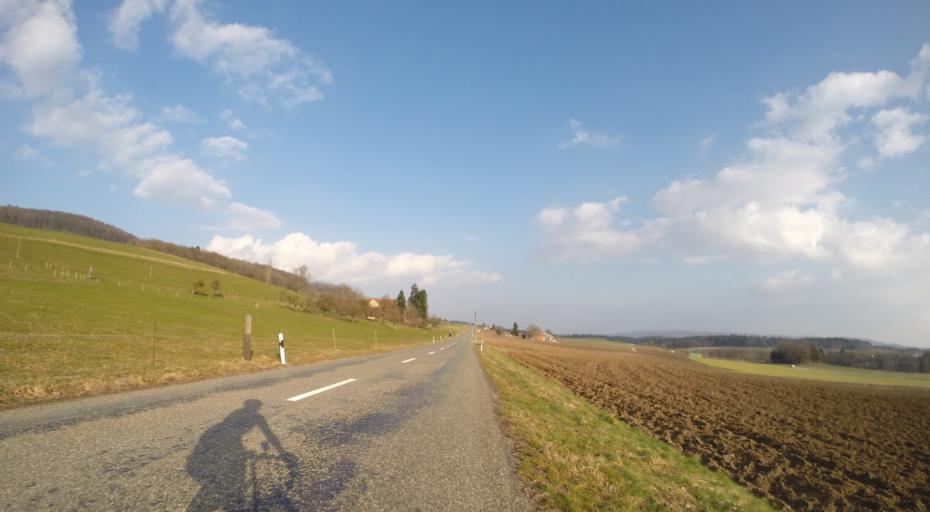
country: CH
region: Thurgau
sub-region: Frauenfeld District
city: Huttwilen
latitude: 47.6035
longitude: 8.8856
